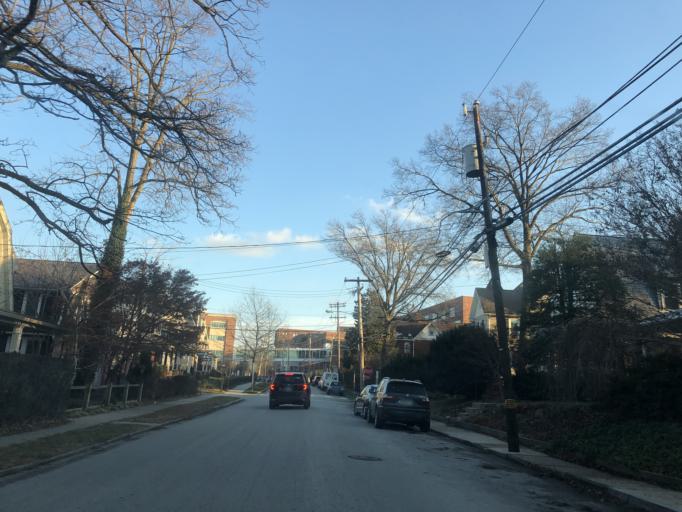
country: US
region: Pennsylvania
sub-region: Montgomery County
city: Bryn Mawr
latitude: 40.0211
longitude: -75.3239
